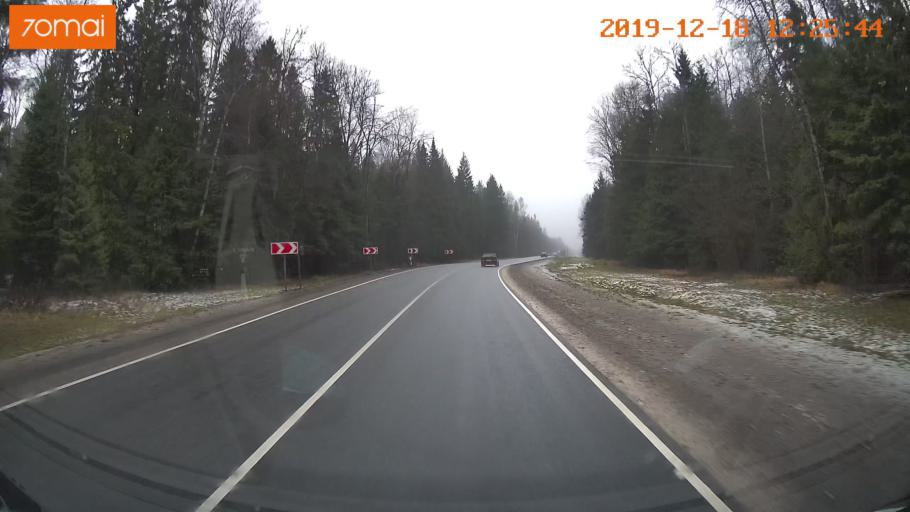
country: RU
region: Moskovskaya
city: Novopetrovskoye
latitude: 56.0423
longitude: 36.4989
